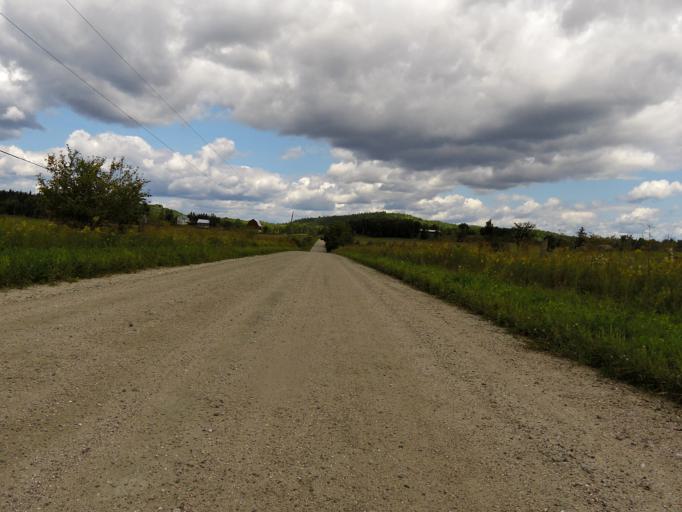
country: CA
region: Quebec
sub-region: Outaouais
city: Wakefield
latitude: 45.7861
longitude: -76.0275
